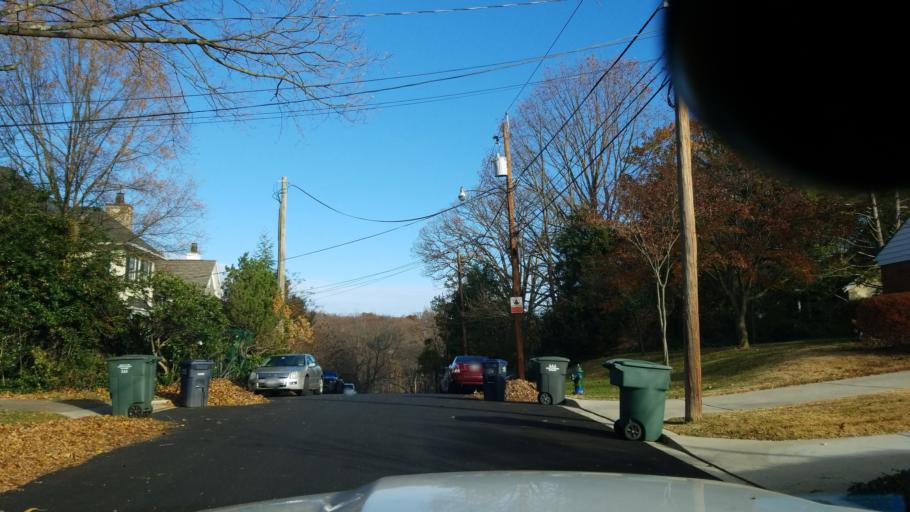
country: US
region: Maryland
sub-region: Montgomery County
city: Brookmont
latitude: 38.9208
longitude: -77.0956
